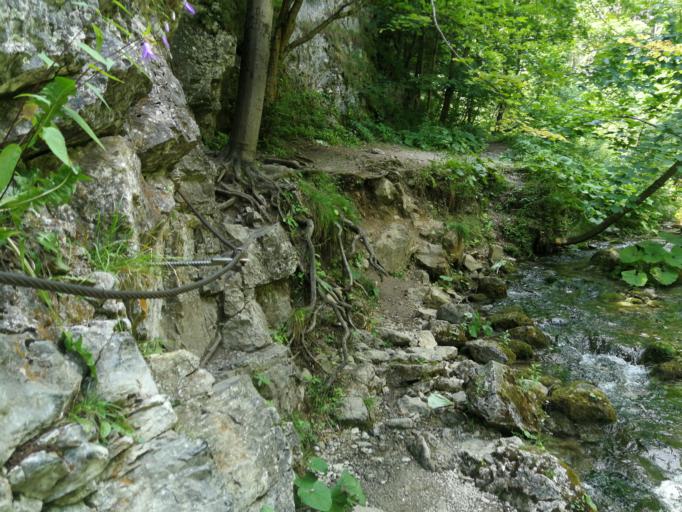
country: SK
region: Zilinsky
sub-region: Okres Liptovsky Mikulas
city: Liptovsky Mikulas
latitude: 49.1613
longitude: 19.4943
